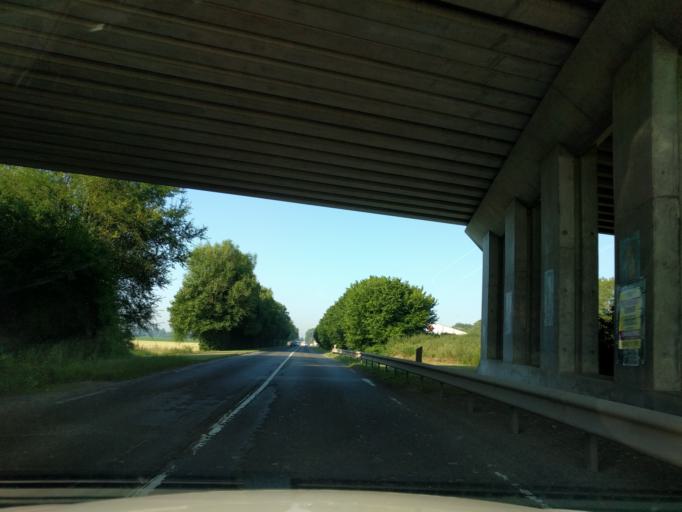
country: FR
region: Picardie
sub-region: Departement de la Somme
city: Chaulnes
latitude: 49.8428
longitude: 2.8709
